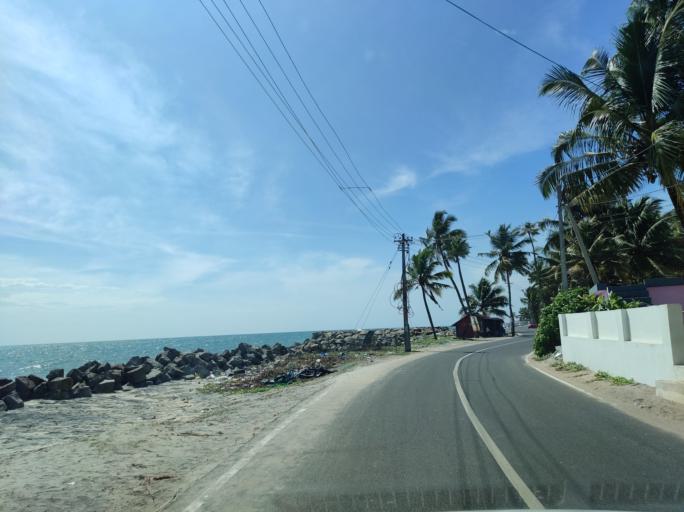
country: IN
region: Kerala
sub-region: Alappuzha
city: Kayankulam
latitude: 9.2074
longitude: 76.4311
